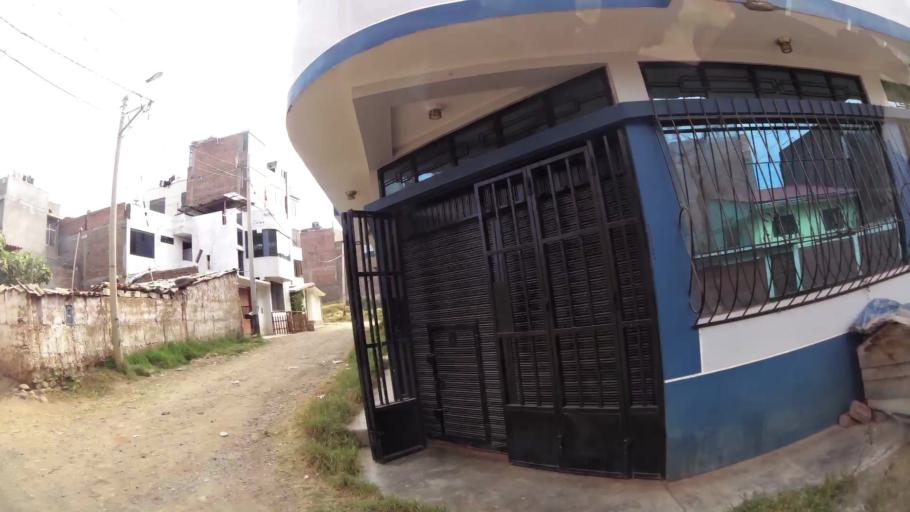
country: PE
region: Junin
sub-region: Provincia de Huancayo
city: Huancayo
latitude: -12.0531
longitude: -75.1982
